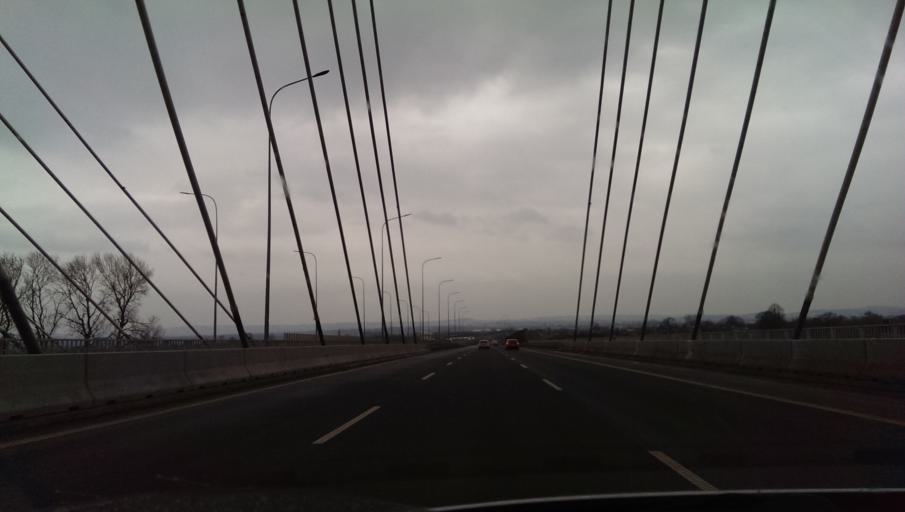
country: PL
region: Lesser Poland Voivodeship
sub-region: Powiat wielicki
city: Kokotow
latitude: 50.0500
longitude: 20.0721
